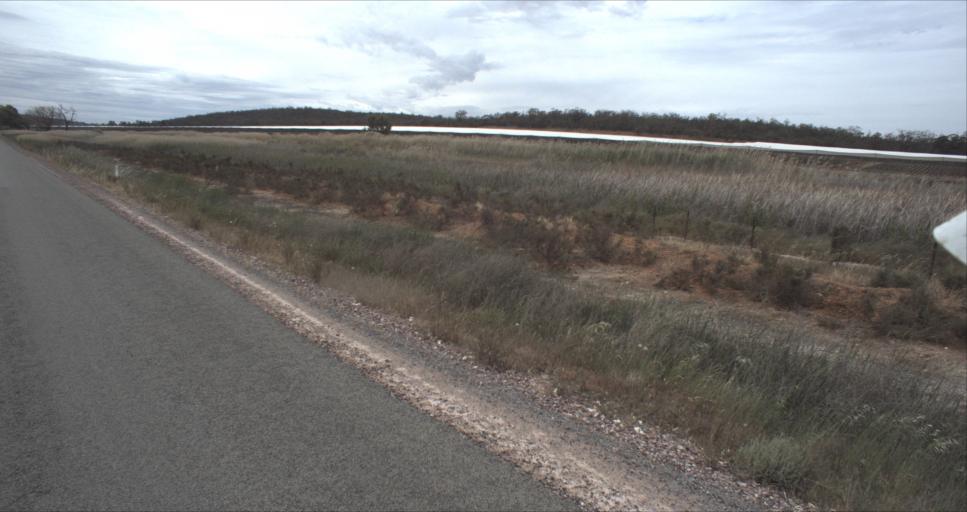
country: AU
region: New South Wales
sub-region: Leeton
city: Leeton
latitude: -34.4332
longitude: 146.3768
